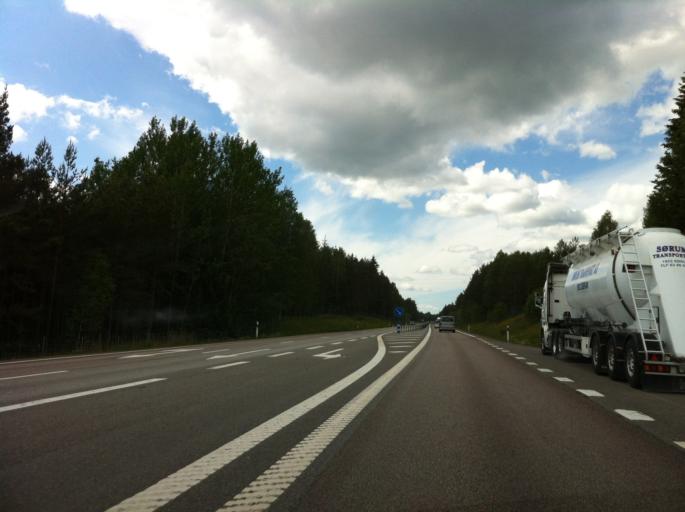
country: SE
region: Vaestra Goetaland
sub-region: Amals Kommun
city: Amal
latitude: 59.1103
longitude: 12.8073
